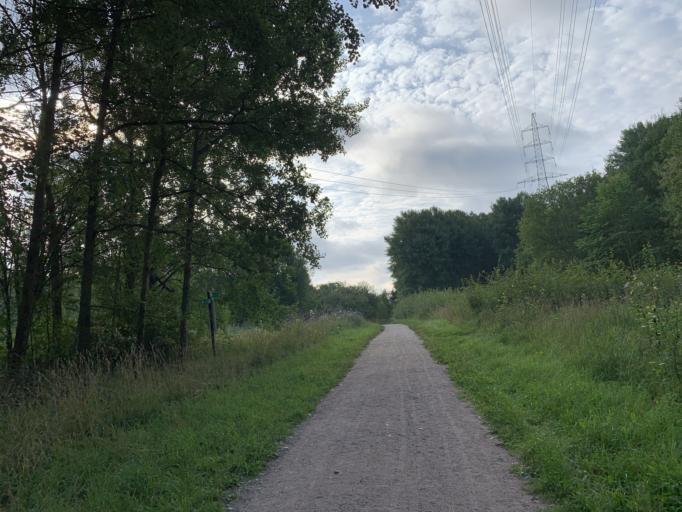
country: SE
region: Stockholm
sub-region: Solna Kommun
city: Rasunda
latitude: 59.3901
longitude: 17.9876
